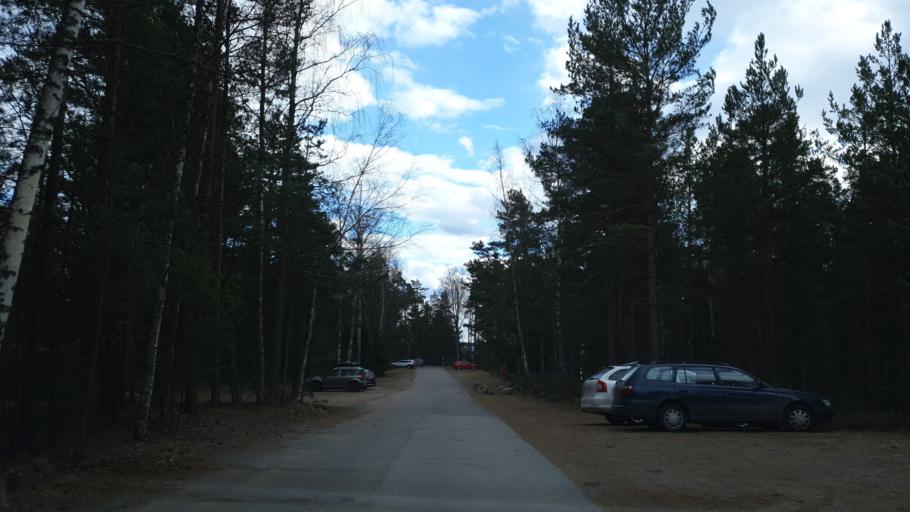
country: SE
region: Stockholm
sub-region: Varmdo Kommun
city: Hemmesta
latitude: 59.2179
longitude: 18.5243
